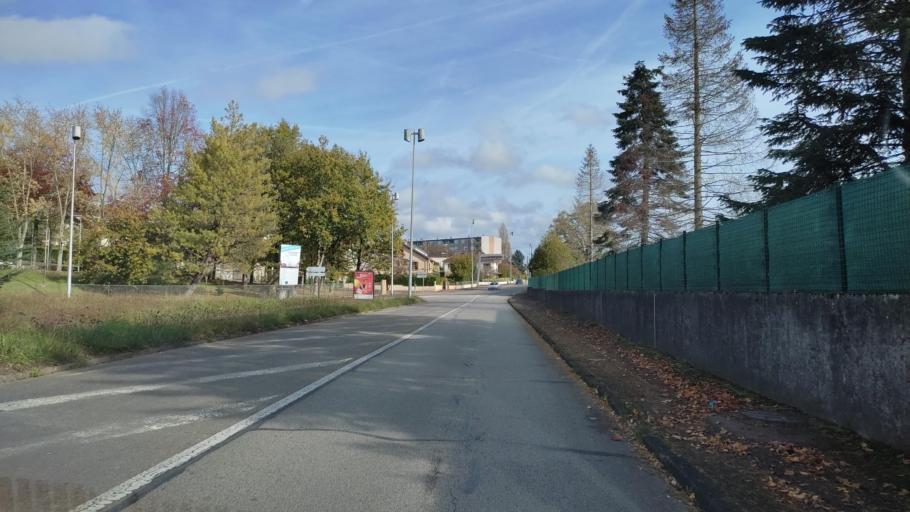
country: FR
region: Limousin
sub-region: Departement de la Haute-Vienne
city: Isle
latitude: 45.8166
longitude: 1.2352
